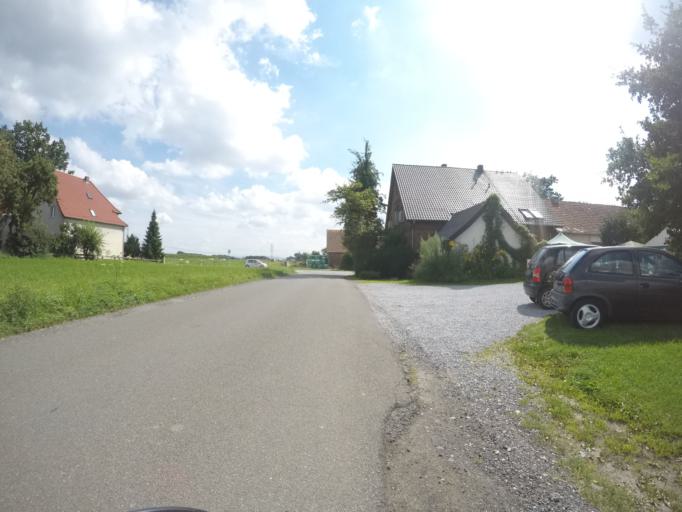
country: DE
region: North Rhine-Westphalia
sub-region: Regierungsbezirk Detmold
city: Hiddenhausen
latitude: 52.1370
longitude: 8.6052
